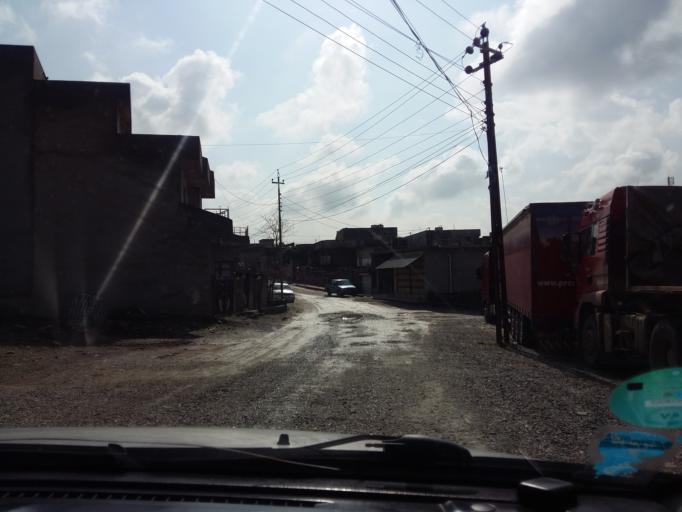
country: IQ
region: As Sulaymaniyah
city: Qeladize
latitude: 36.1918
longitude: 45.1234
